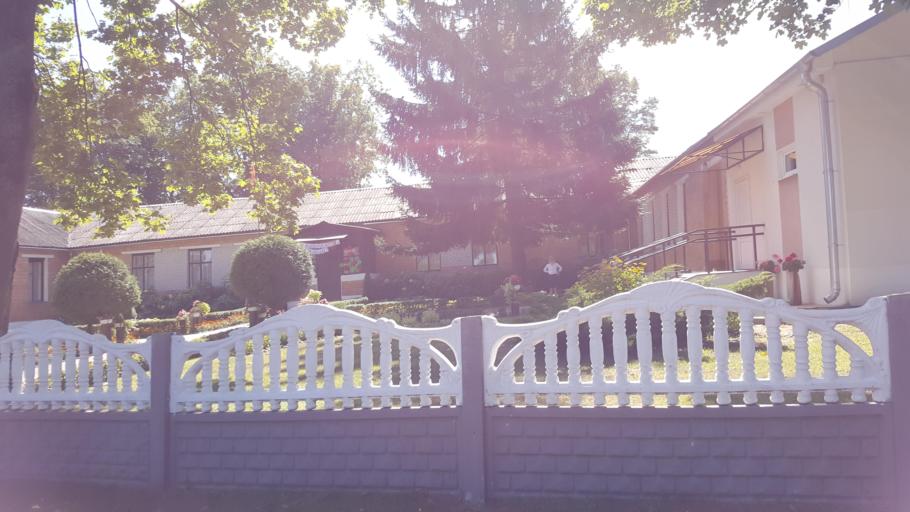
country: BY
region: Brest
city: Vysokaye
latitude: 52.2634
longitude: 23.4061
